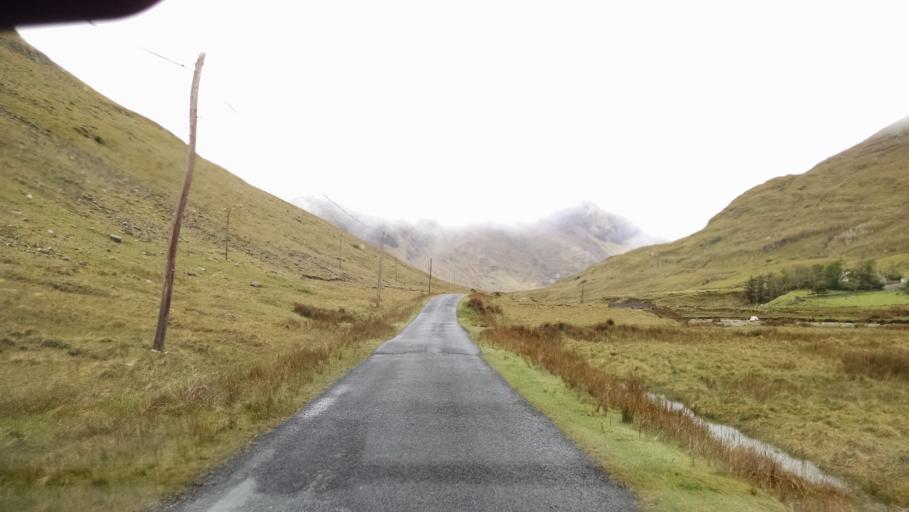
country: IE
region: Connaught
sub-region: Maigh Eo
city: Westport
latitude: 53.6460
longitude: -9.7269
